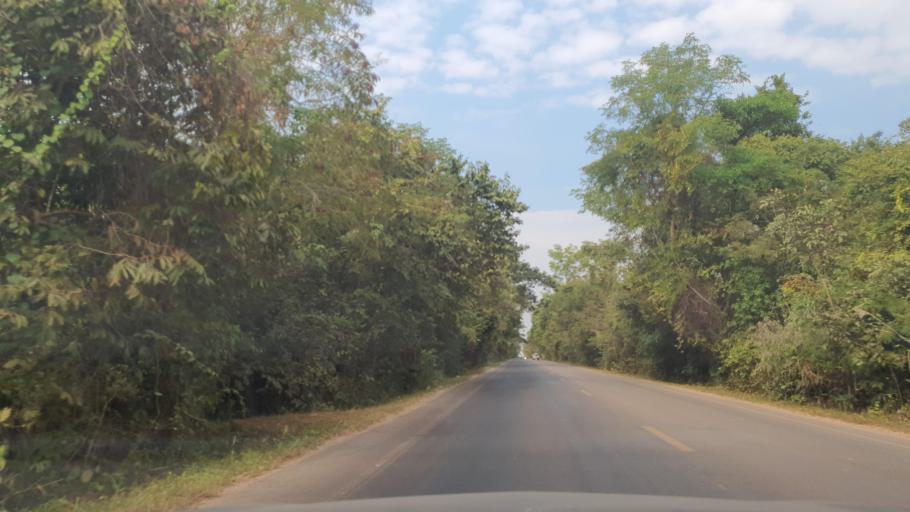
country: TH
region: Changwat Bueng Kan
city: Si Wilai
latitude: 18.2863
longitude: 103.8253
